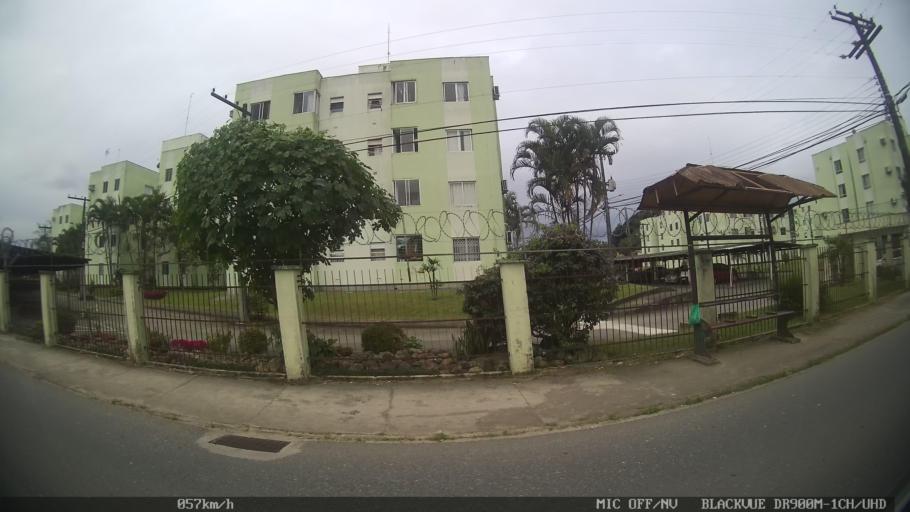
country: BR
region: Santa Catarina
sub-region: Joinville
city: Joinville
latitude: -26.2783
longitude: -48.8745
